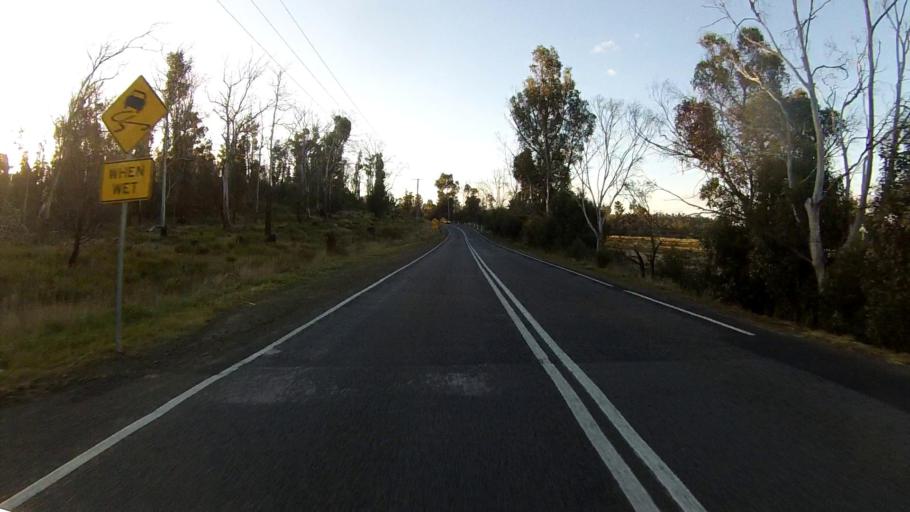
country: AU
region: Tasmania
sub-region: Sorell
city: Sorell
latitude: -42.8596
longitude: 147.8233
